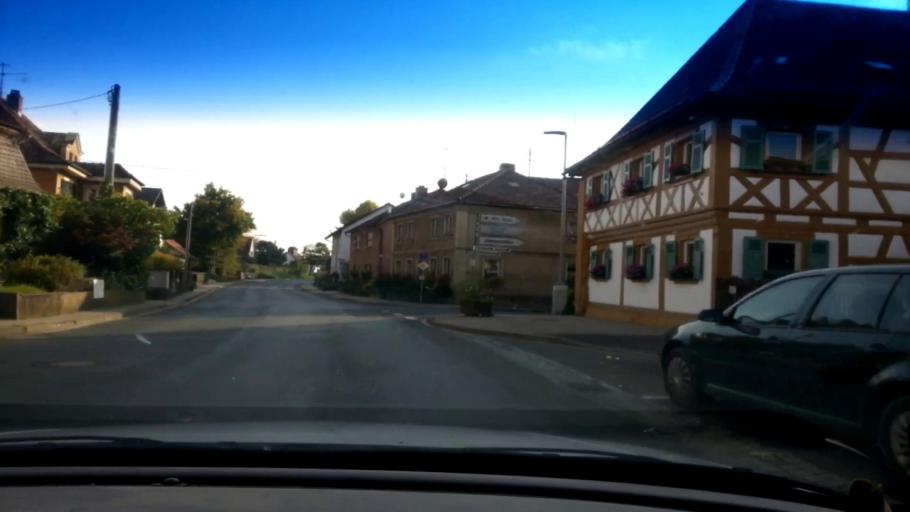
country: DE
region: Bavaria
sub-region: Upper Franconia
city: Schesslitz
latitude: 49.9750
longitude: 11.0296
